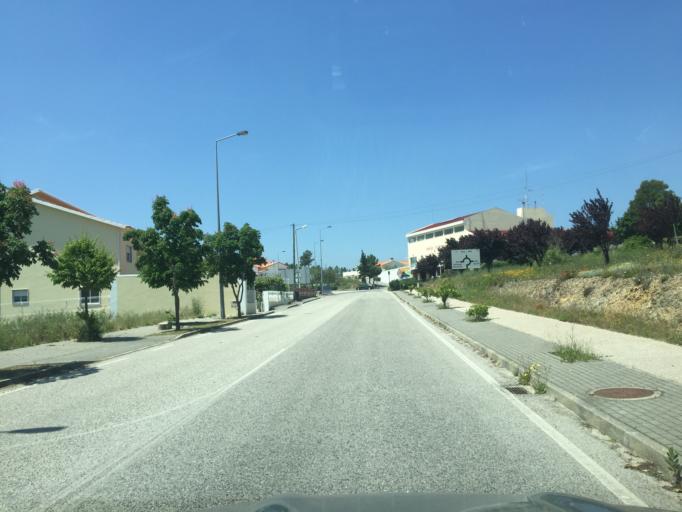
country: PT
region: Castelo Branco
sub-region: Vila de Rei
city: Vila de Rei
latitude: 39.6765
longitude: -8.1403
